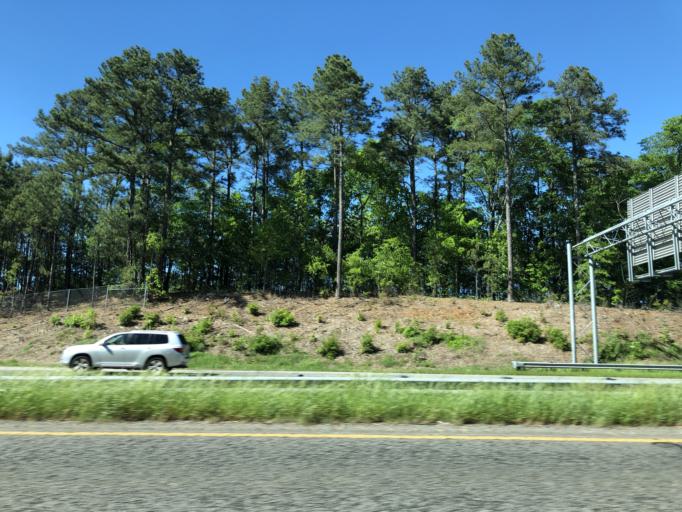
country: US
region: Georgia
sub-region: Clarke County
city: Country Club Estates
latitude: 33.9719
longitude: -83.4099
